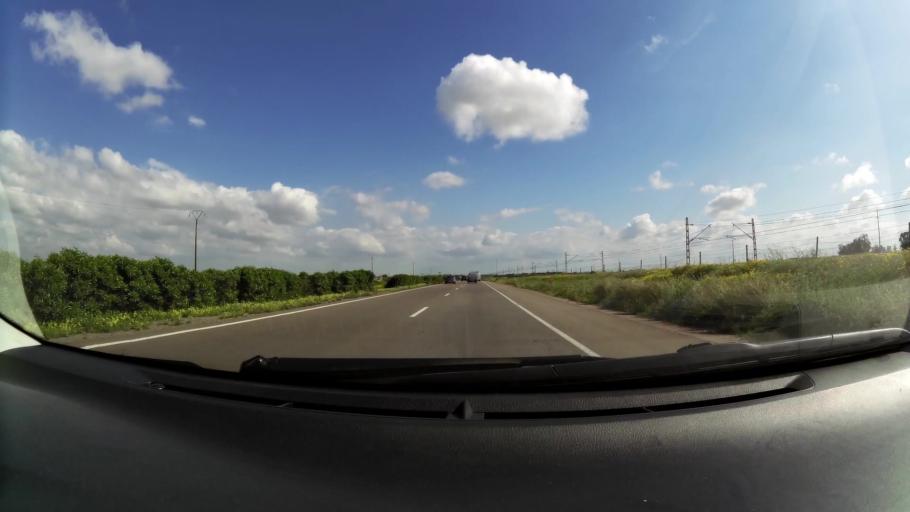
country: MA
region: Chaouia-Ouardigha
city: Nouaseur
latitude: 33.3518
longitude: -7.6163
